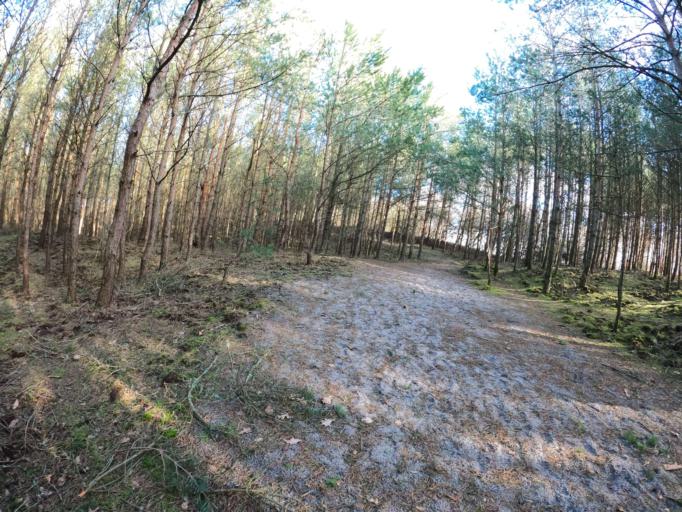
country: PL
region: West Pomeranian Voivodeship
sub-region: Powiat koszalinski
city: Sianow
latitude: 54.3212
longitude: 16.2178
